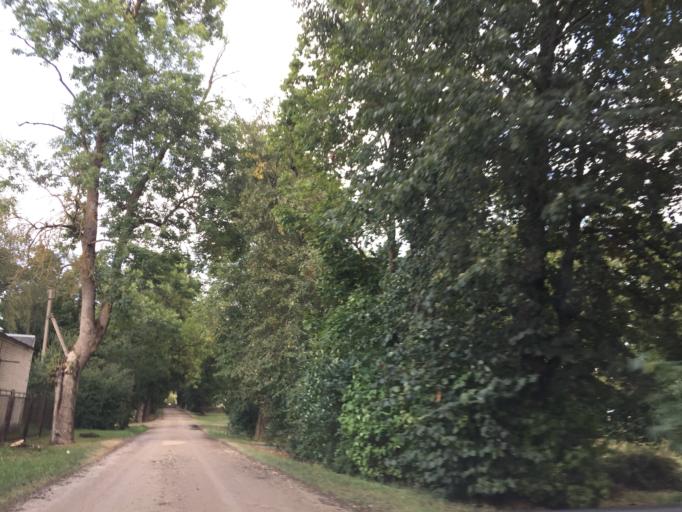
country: LT
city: Zagare
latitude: 56.3633
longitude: 23.2670
